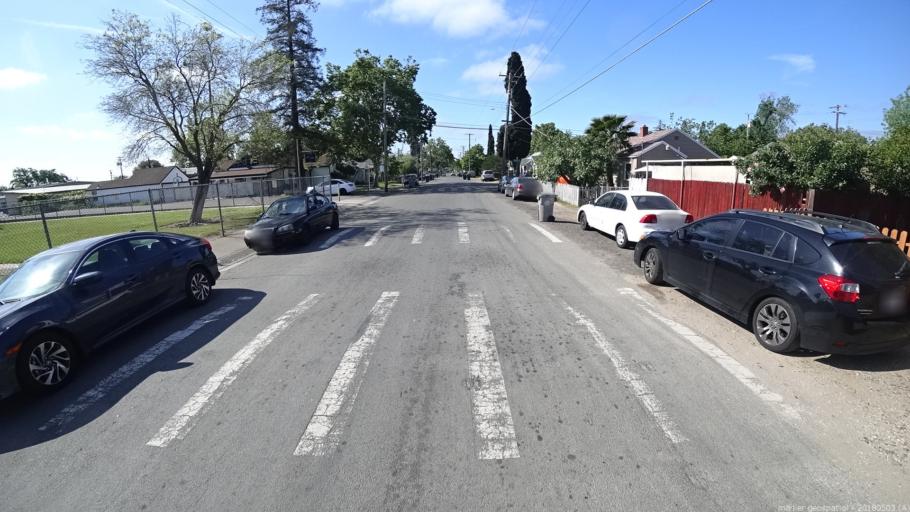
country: US
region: California
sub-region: Sacramento County
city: Arden-Arcade
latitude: 38.6134
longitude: -121.4381
